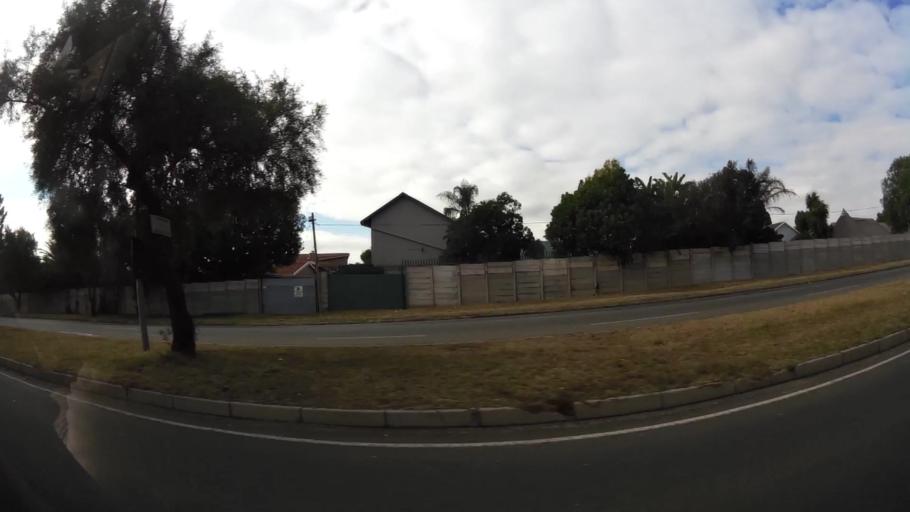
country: ZA
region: Gauteng
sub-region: City of Johannesburg Metropolitan Municipality
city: Roodepoort
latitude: -26.1152
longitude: 27.8517
